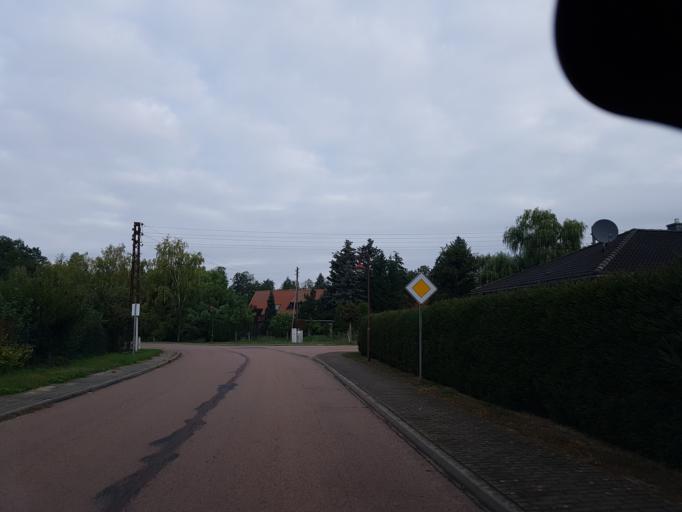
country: DE
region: Saxony-Anhalt
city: Klieken
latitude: 51.9541
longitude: 12.3087
